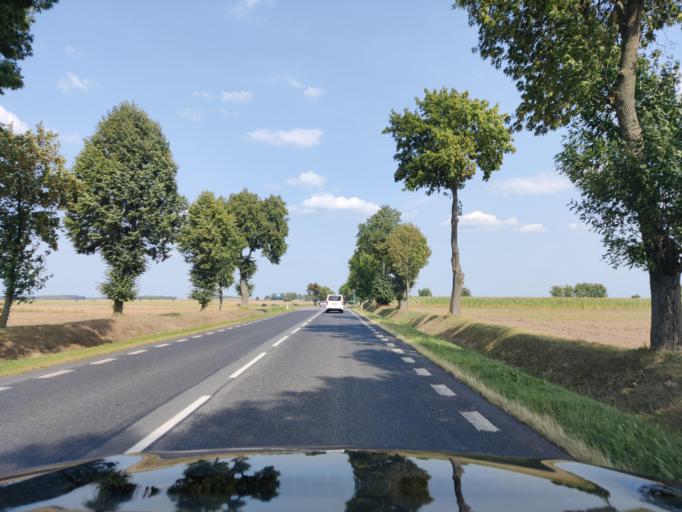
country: PL
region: Masovian Voivodeship
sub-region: Powiat makowski
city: Rzewnie
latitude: 52.8592
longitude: 21.3115
